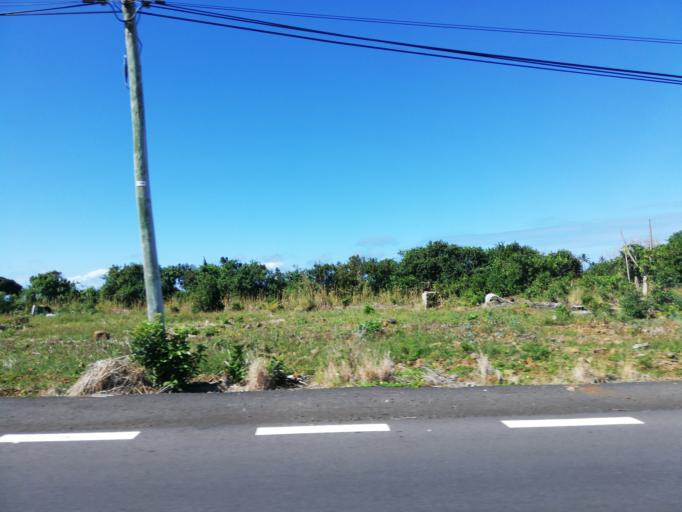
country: MU
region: Grand Port
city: Plaine Magnien
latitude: -20.4435
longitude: 57.6905
